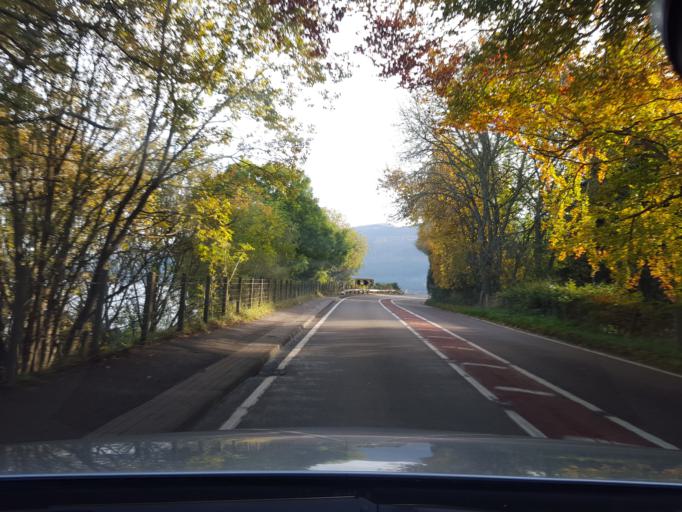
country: GB
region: Scotland
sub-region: Highland
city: Beauly
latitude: 57.3273
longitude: -4.4478
